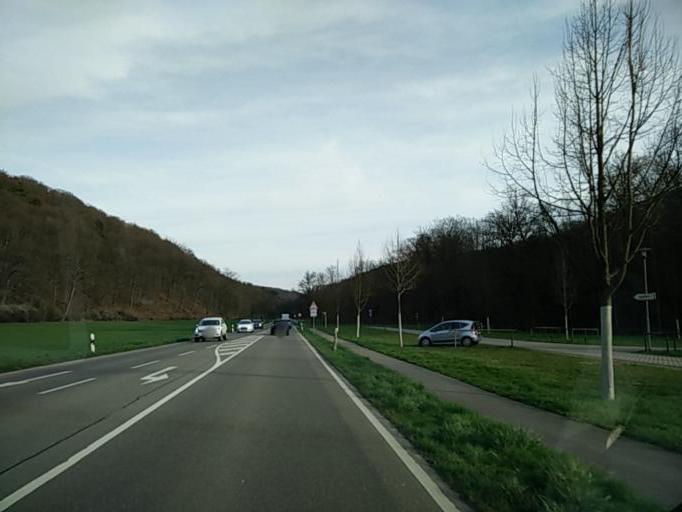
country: DE
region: Baden-Wuerttemberg
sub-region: Tuebingen Region
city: Tuebingen
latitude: 48.5577
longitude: 9.0652
